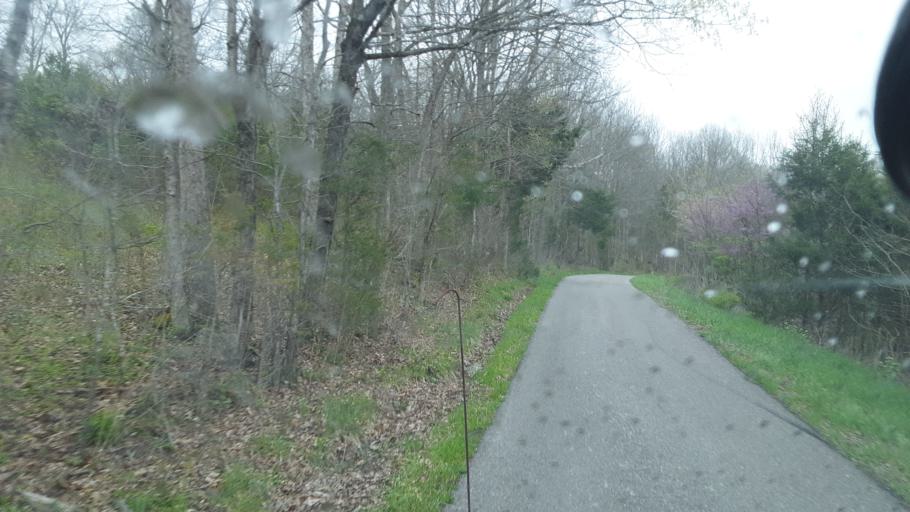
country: US
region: Kentucky
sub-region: Owen County
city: Owenton
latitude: 38.6450
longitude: -84.7853
